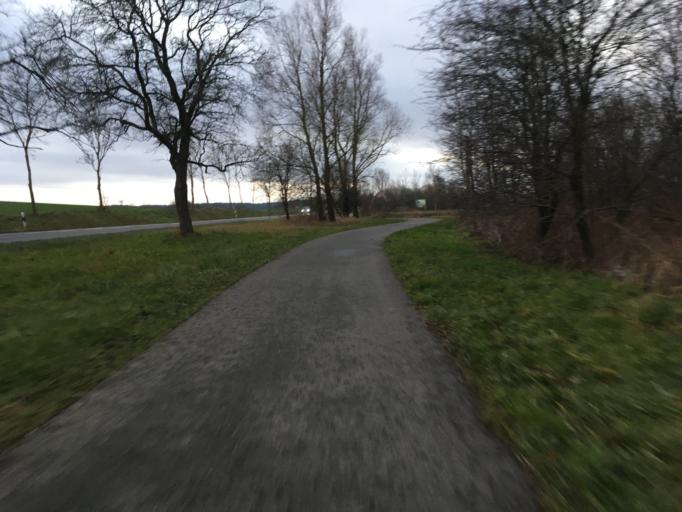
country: DE
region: Mecklenburg-Vorpommern
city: Sagard
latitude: 54.4995
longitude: 13.5839
